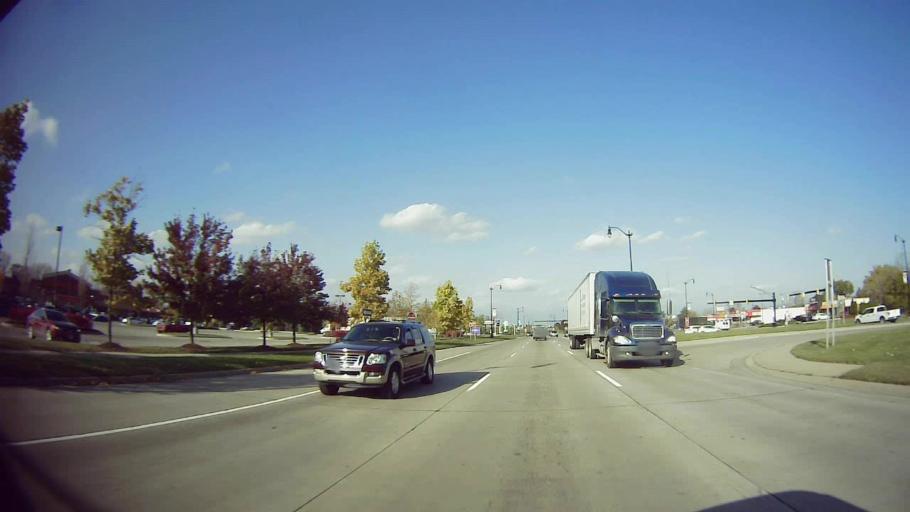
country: US
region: Michigan
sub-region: Wayne County
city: Taylor
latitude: 42.2234
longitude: -83.2693
